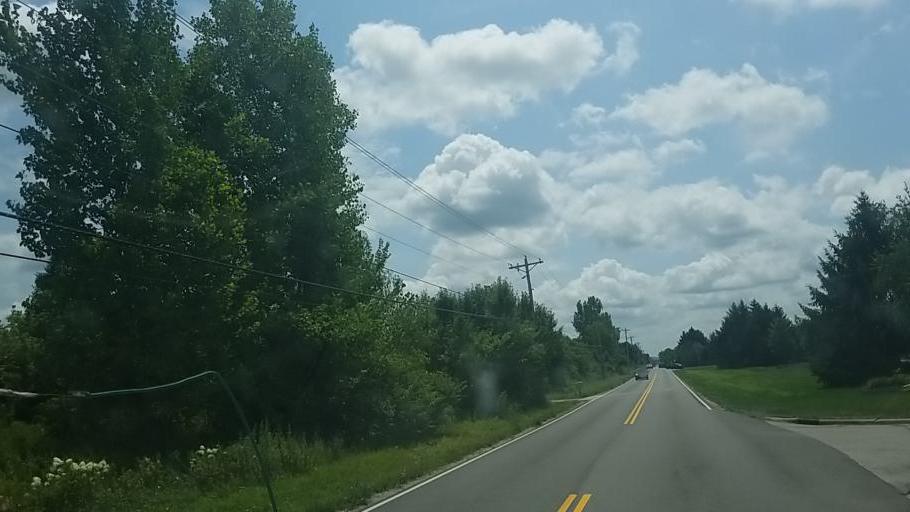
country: US
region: Ohio
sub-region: Fairfield County
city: Pickerington
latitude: 39.9179
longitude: -82.7465
